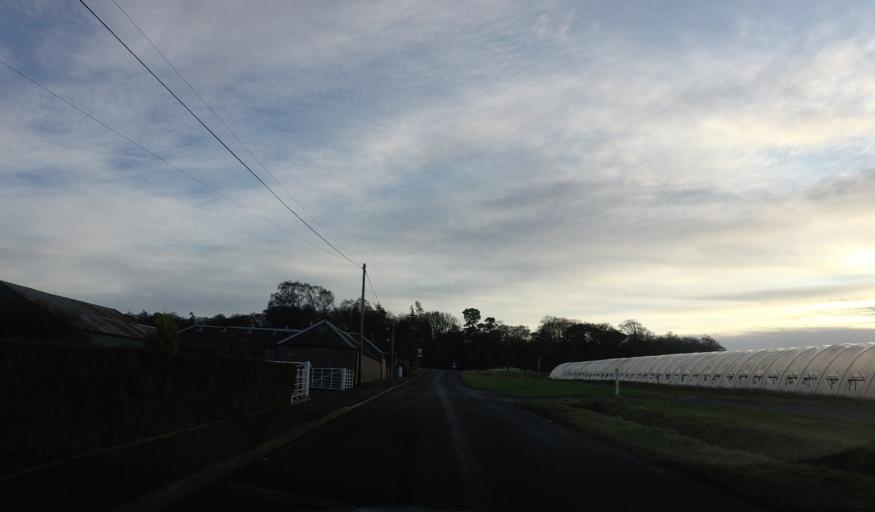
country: GB
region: Scotland
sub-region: Angus
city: Muirhead
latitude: 56.4629
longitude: -3.0878
